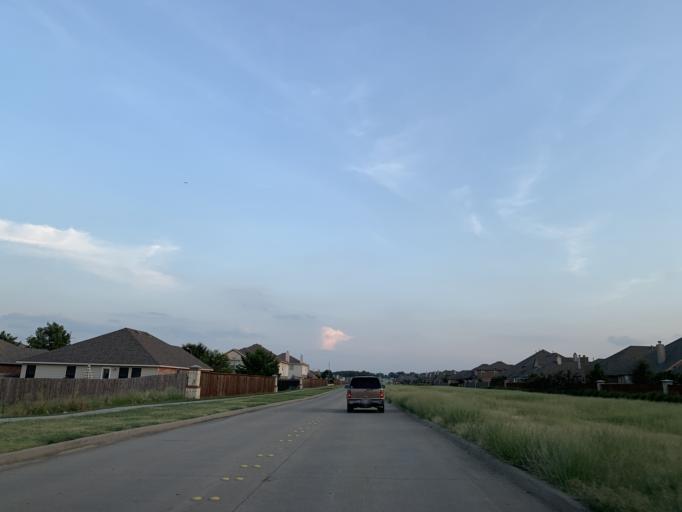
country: US
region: Texas
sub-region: Tarrant County
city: Keller
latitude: 32.9618
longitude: -97.2645
